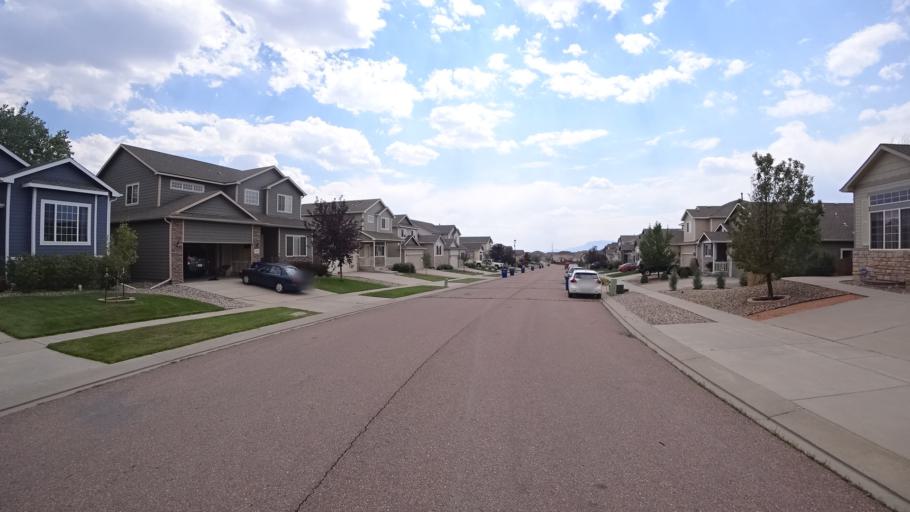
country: US
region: Colorado
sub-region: El Paso County
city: Black Forest
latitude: 38.9474
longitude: -104.6904
